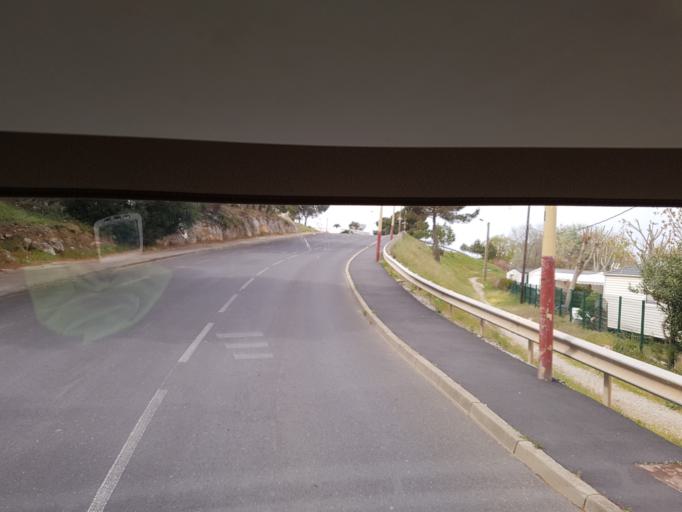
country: FR
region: Languedoc-Roussillon
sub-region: Departement de l'Aude
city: Fleury
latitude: 43.1874
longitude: 3.1978
